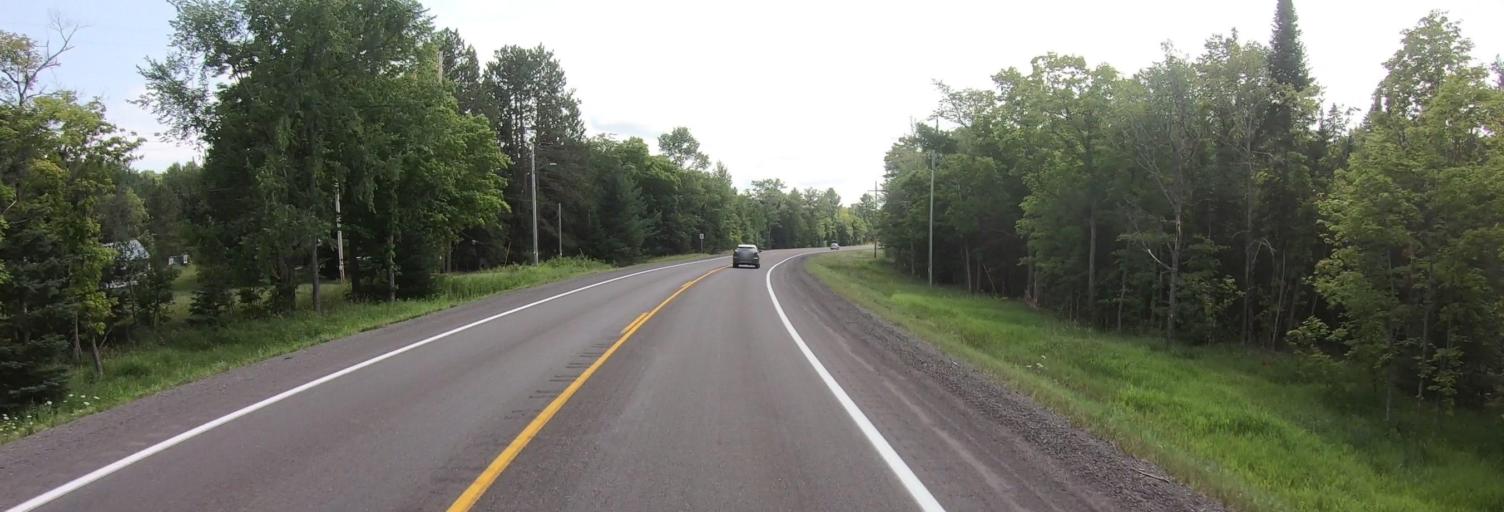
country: US
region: Michigan
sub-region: Houghton County
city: Hancock
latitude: 46.9621
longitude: -88.7764
